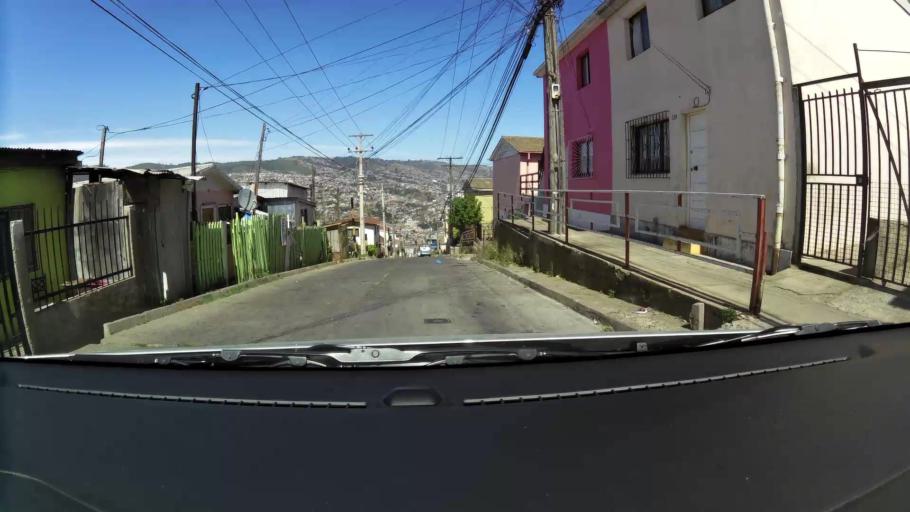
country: CL
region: Valparaiso
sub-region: Provincia de Valparaiso
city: Valparaiso
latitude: -33.0491
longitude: -71.5940
